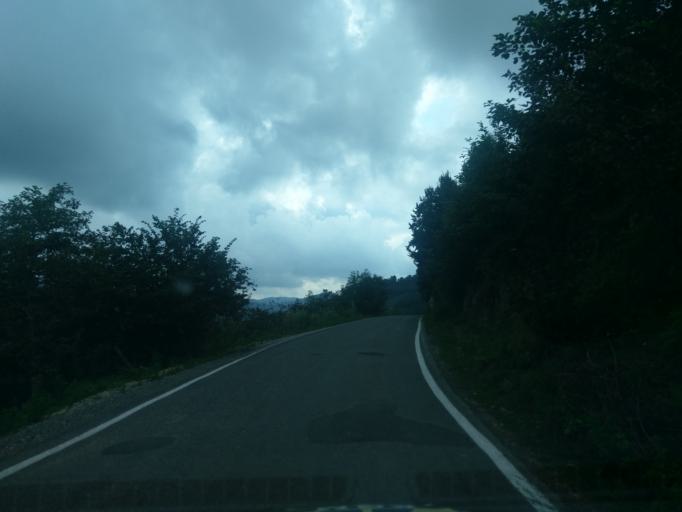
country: TR
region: Ordu
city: Camas
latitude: 40.8888
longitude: 37.6274
